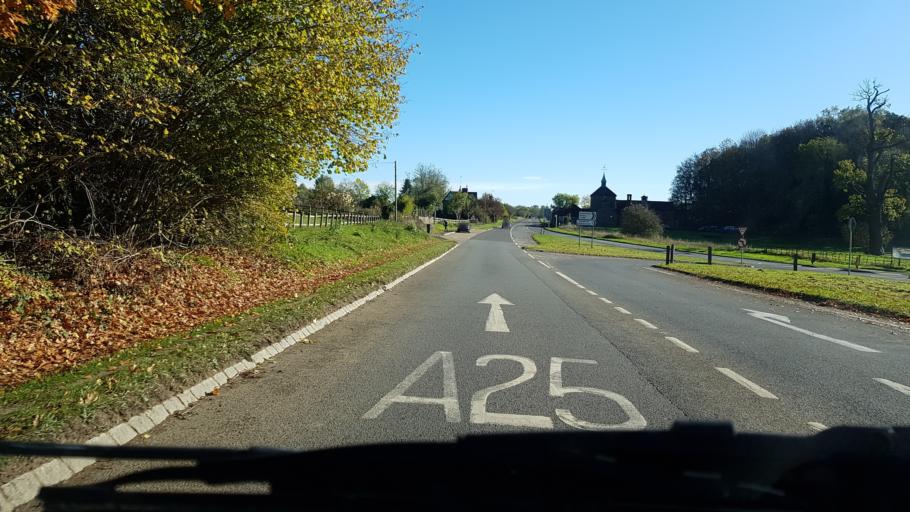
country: GB
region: England
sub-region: Surrey
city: Chilworth
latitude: 51.2252
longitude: -0.4832
